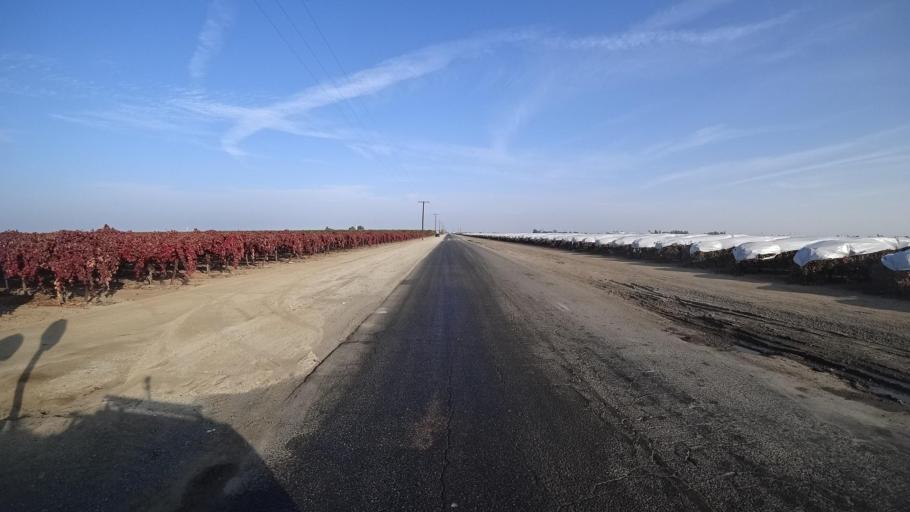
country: US
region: California
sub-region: Kern County
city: Delano
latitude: 35.7616
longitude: -119.1875
